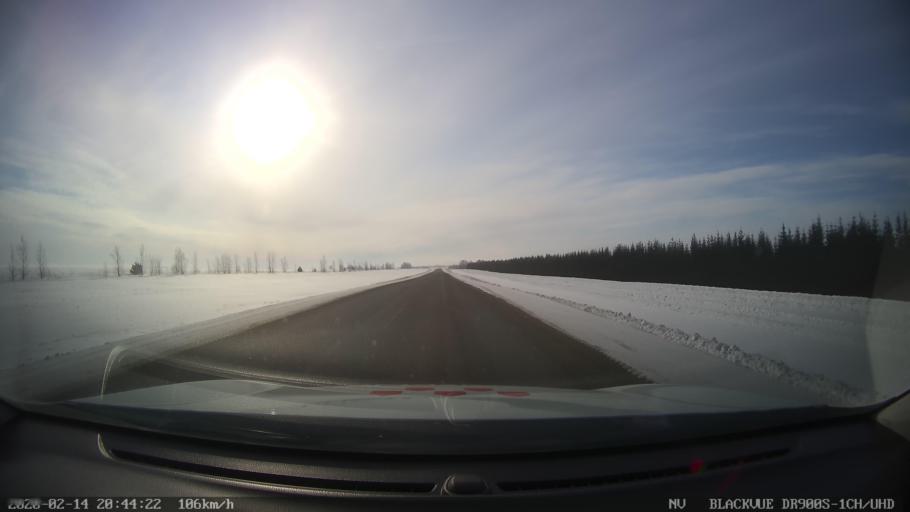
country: RU
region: Tatarstan
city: Kuybyshevskiy Zaton
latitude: 55.2948
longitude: 49.1464
